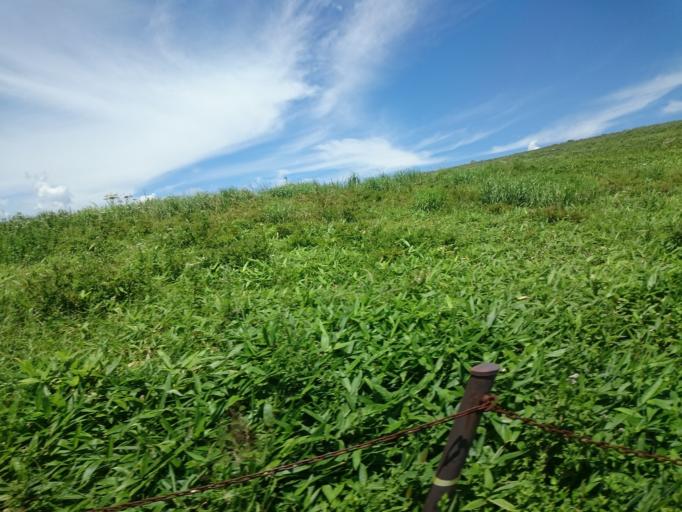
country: JP
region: Nagano
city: Suwa
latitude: 36.1013
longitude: 138.1827
